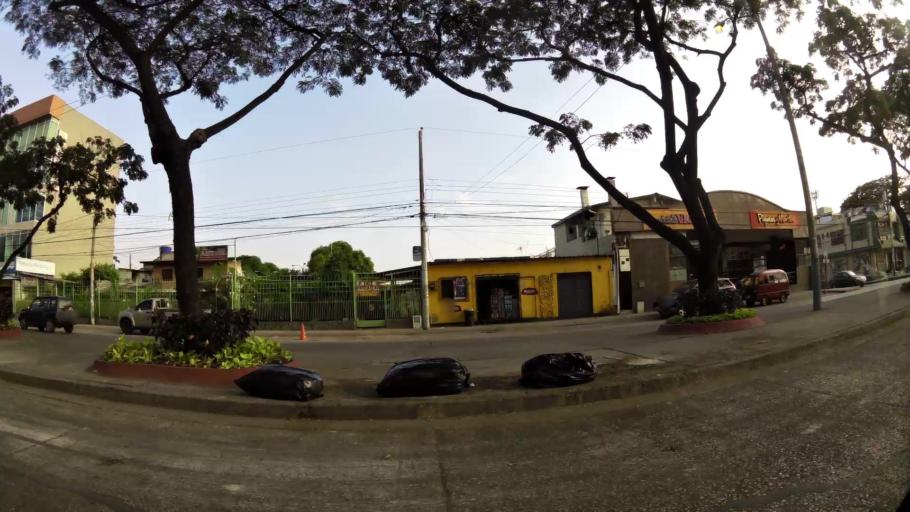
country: EC
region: Guayas
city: Eloy Alfaro
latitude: -2.1332
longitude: -79.9047
